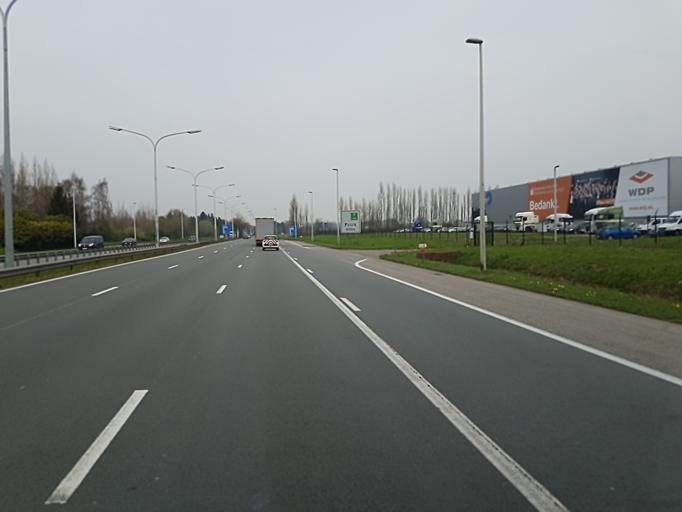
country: BE
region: Flanders
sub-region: Provincie Antwerpen
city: Willebroek
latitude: 51.0525
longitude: 4.3360
